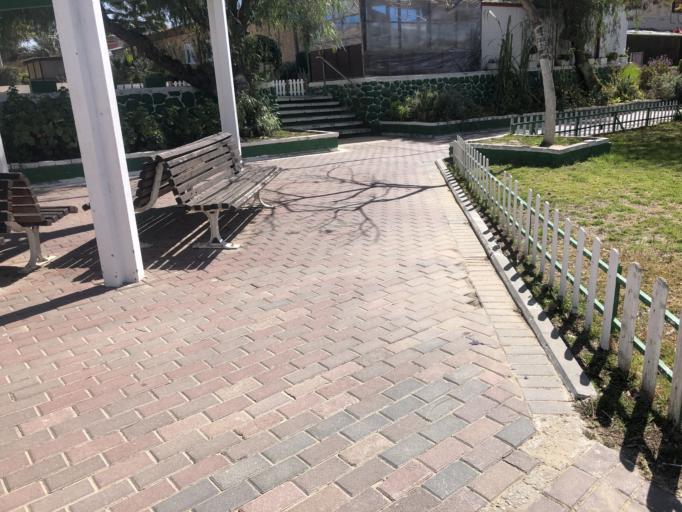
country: IL
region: Southern District
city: Dimona
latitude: 31.0674
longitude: 35.0401
